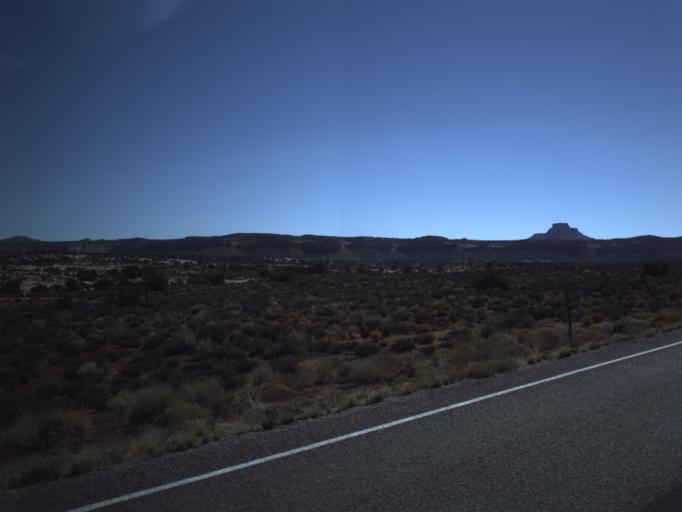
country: US
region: Utah
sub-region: San Juan County
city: Blanding
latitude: 37.7857
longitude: -110.2952
